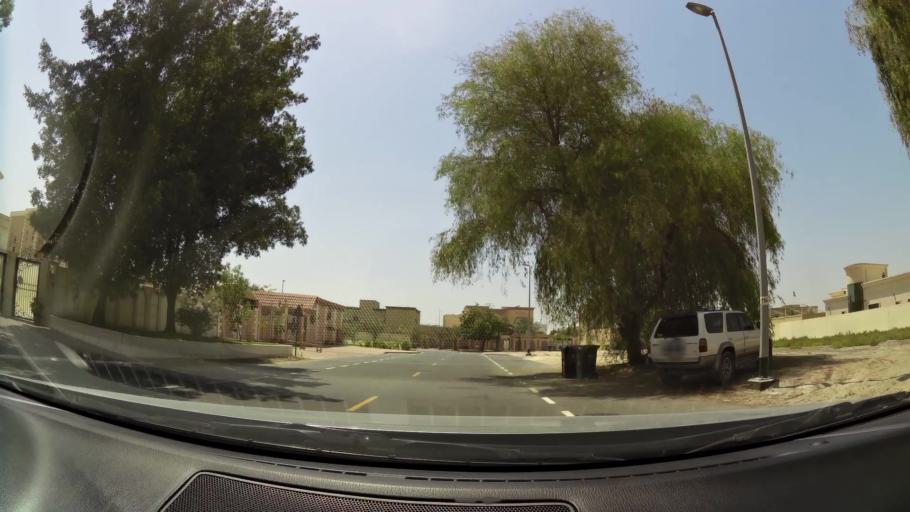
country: AE
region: Dubai
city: Dubai
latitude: 25.1047
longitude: 55.2177
